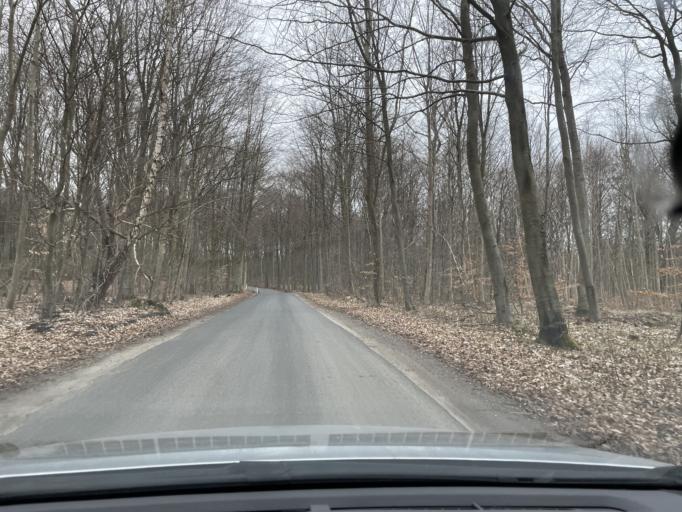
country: DK
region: South Denmark
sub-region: Nyborg Kommune
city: Nyborg
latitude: 55.3407
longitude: 10.8003
